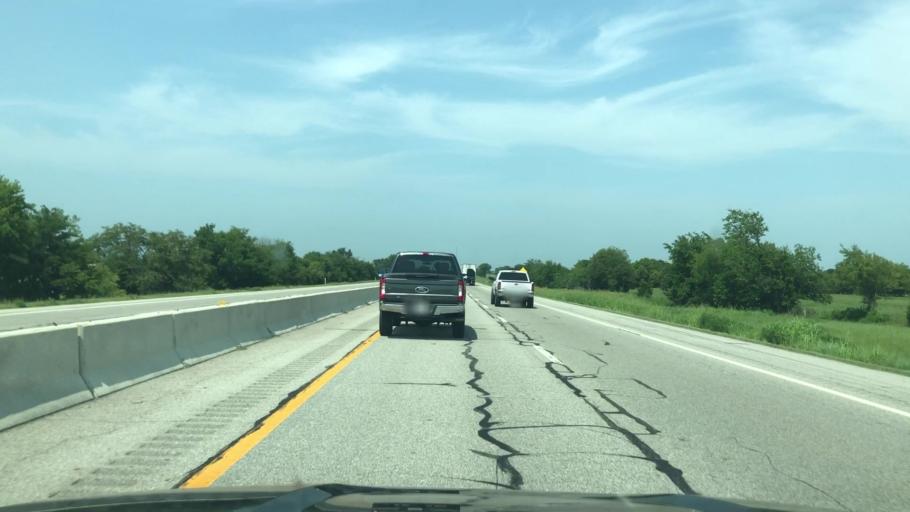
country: US
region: Oklahoma
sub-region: Ottawa County
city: Fairland
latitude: 36.7816
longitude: -94.8893
